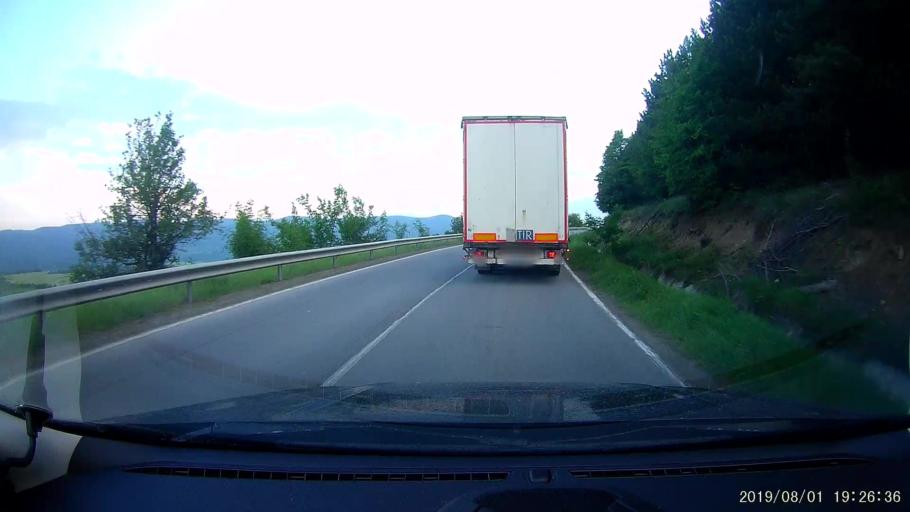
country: BG
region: Burgas
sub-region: Obshtina Sungurlare
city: Sungurlare
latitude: 42.8560
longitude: 26.9396
